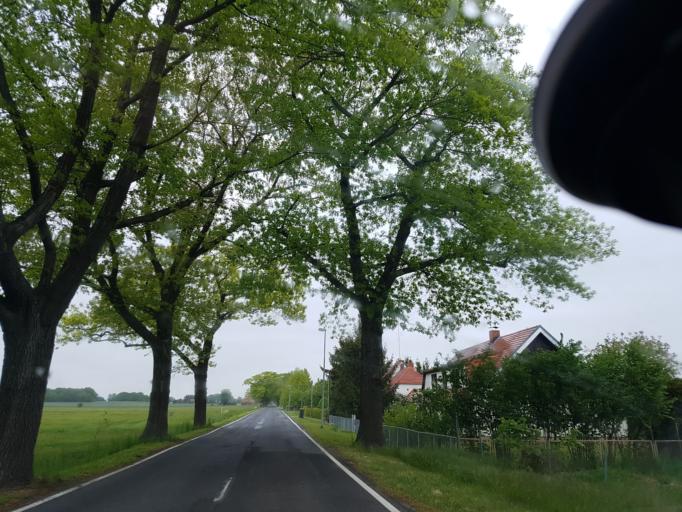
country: DE
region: Brandenburg
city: Cottbus
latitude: 51.6690
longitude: 14.3474
